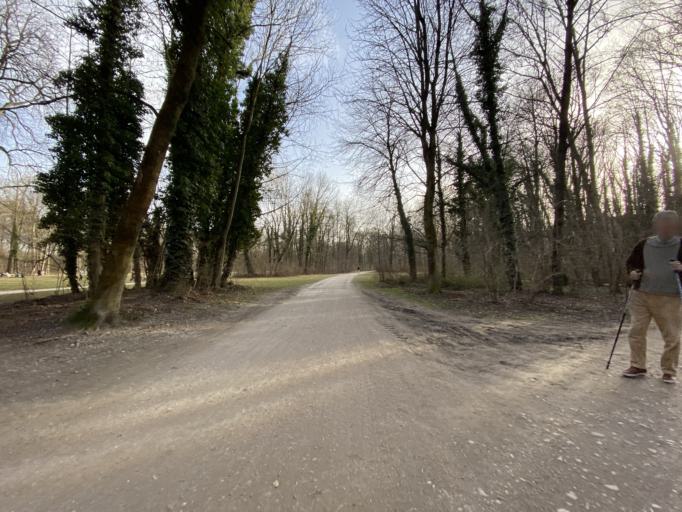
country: DE
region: Bavaria
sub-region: Upper Bavaria
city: Bogenhausen
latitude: 48.1643
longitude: 11.6010
